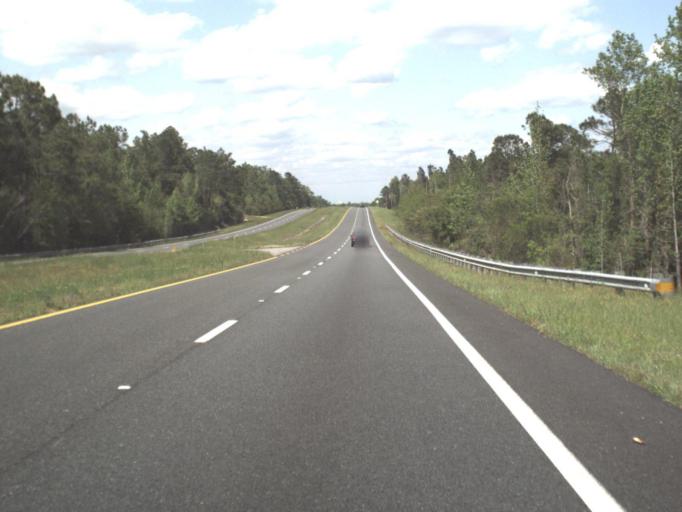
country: US
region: Florida
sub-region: Escambia County
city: Molino
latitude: 30.8323
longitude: -87.3304
